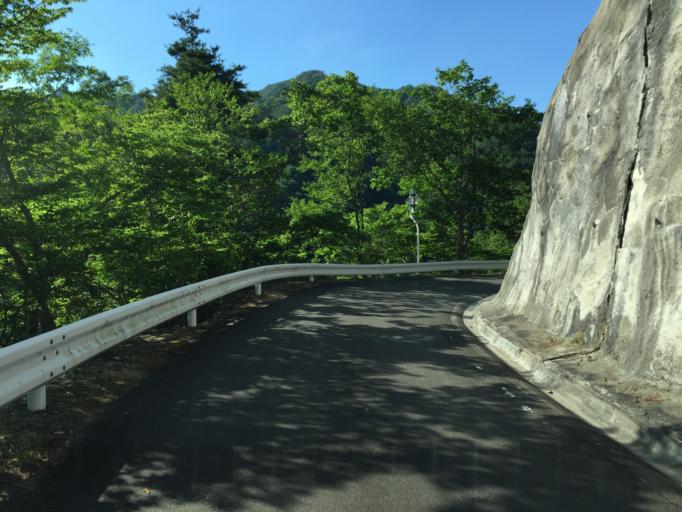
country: JP
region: Yamagata
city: Takahata
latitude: 37.9532
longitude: 140.3447
